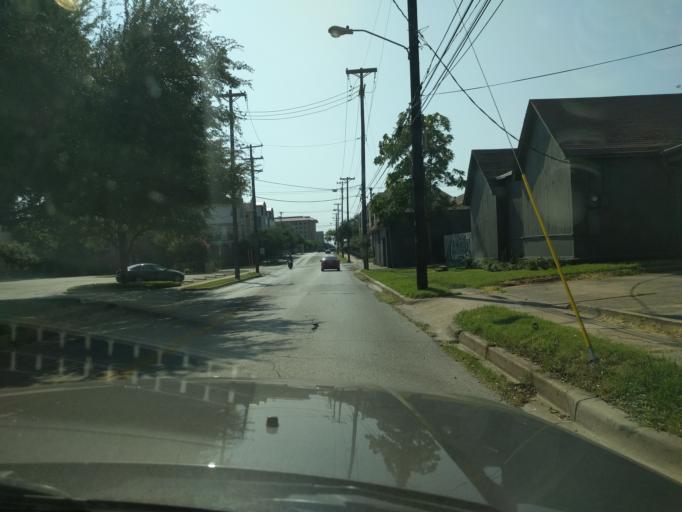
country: US
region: Texas
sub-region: Dallas County
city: Dallas
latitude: 32.7960
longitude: -96.7841
